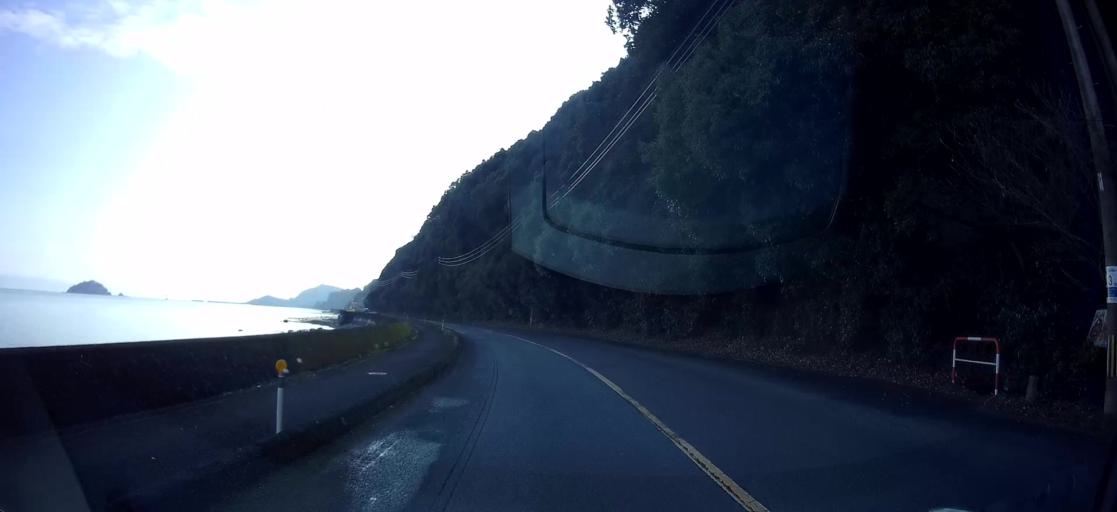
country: JP
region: Kumamoto
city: Yatsushiro
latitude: 32.4862
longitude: 130.4375
